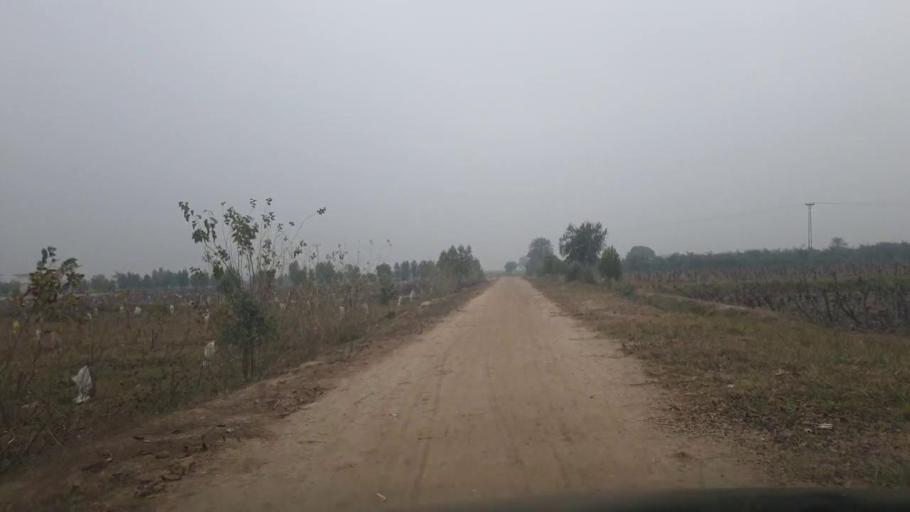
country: PK
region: Sindh
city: Tando Adam
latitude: 25.7680
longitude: 68.6403
